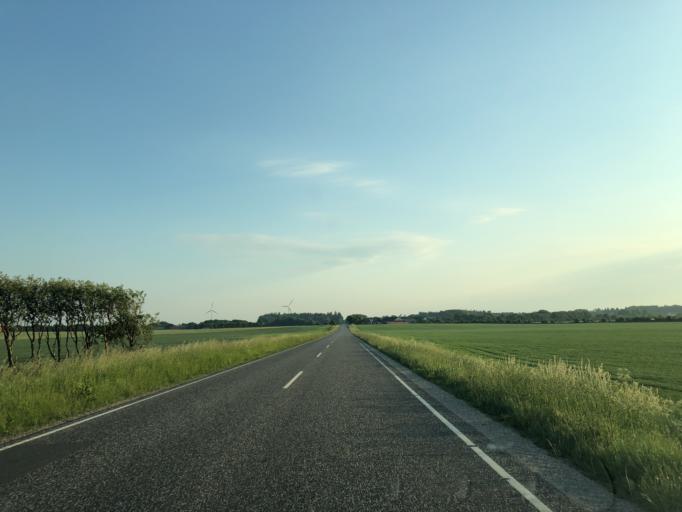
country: DK
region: Central Jutland
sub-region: Struer Kommune
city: Struer
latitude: 56.4382
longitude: 8.5260
